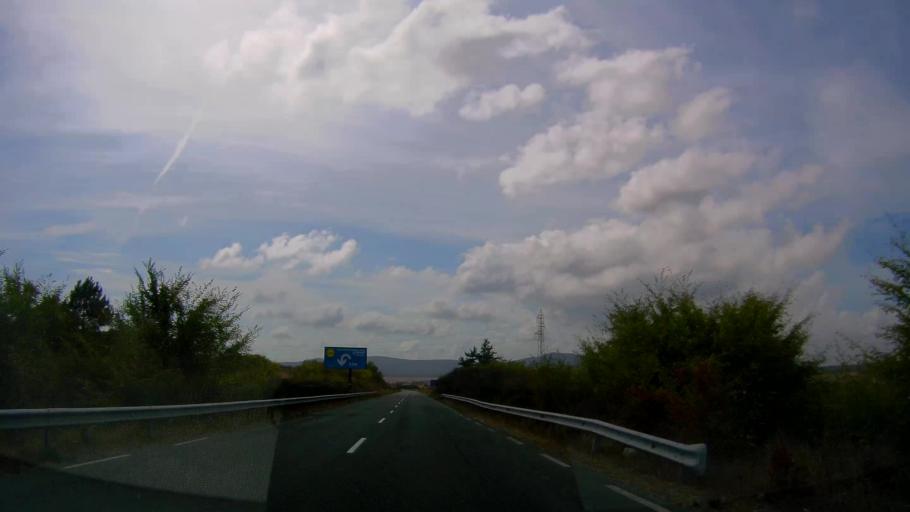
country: BG
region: Burgas
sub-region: Obshtina Sozopol
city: Sozopol
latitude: 42.3998
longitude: 27.6755
